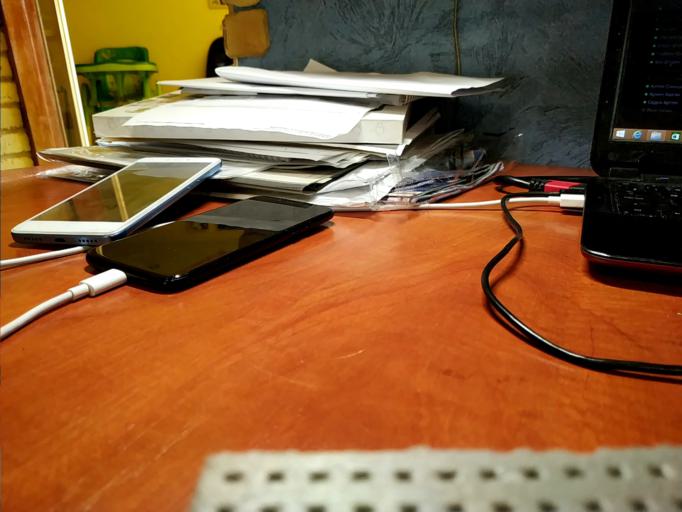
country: RU
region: Tverskaya
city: Spirovo
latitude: 57.4261
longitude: 35.0733
